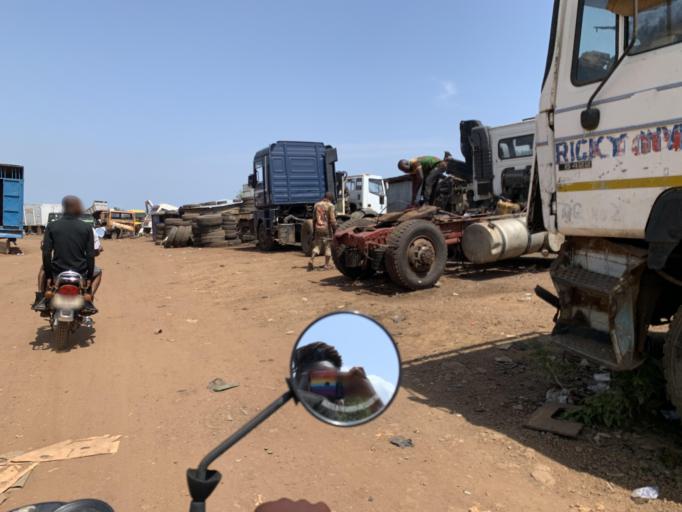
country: SL
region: Western Area
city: Hastings
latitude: 8.3899
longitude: -13.1336
